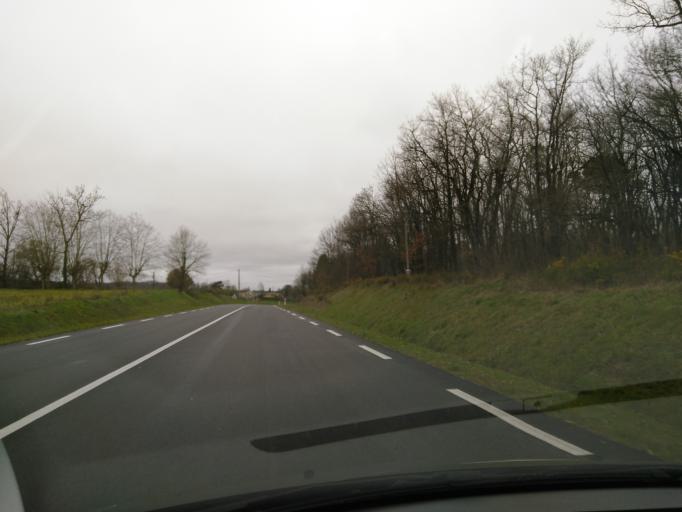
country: FR
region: Aquitaine
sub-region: Departement de la Dordogne
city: Monbazillac
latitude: 44.7350
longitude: 0.5451
